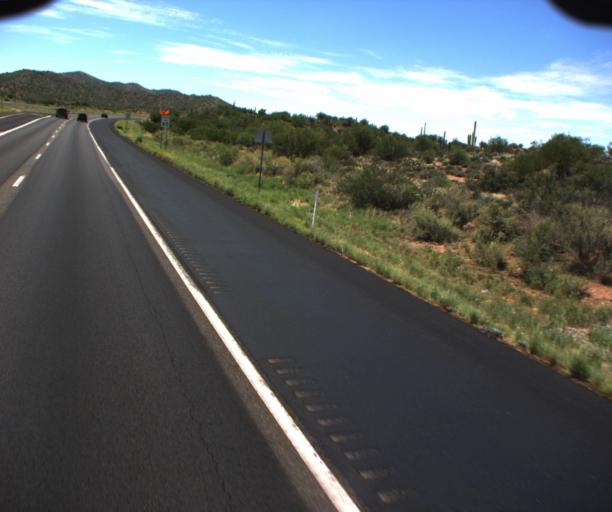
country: US
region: Arizona
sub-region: Pinal County
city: Superior
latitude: 33.2746
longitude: -111.1840
